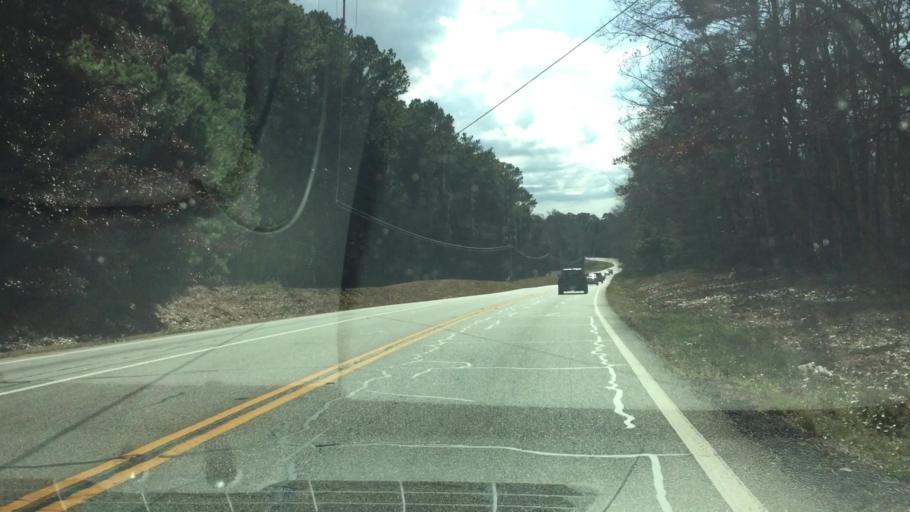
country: US
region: Georgia
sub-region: Henry County
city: McDonough
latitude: 33.4908
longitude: -84.1442
